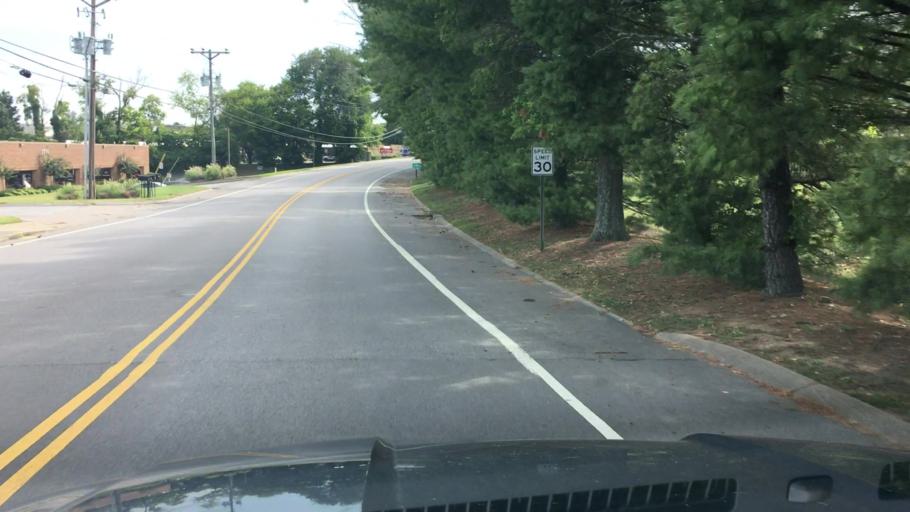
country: US
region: Tennessee
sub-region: Williamson County
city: Franklin
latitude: 35.9675
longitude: -86.8187
